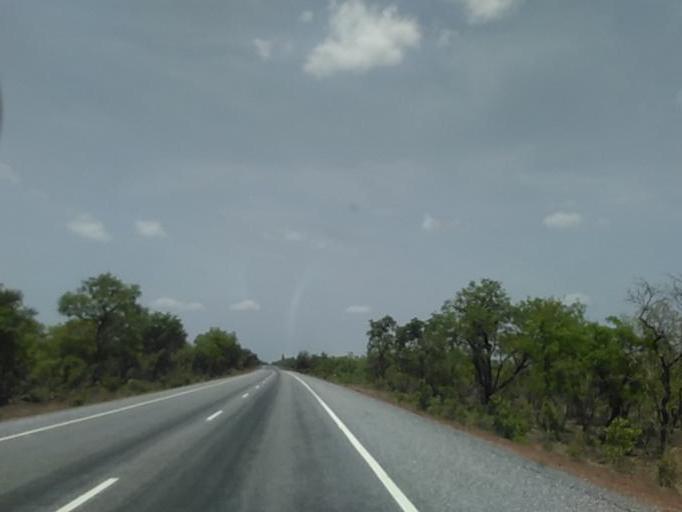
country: GH
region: Northern
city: Tamale
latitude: 9.1458
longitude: -1.3704
